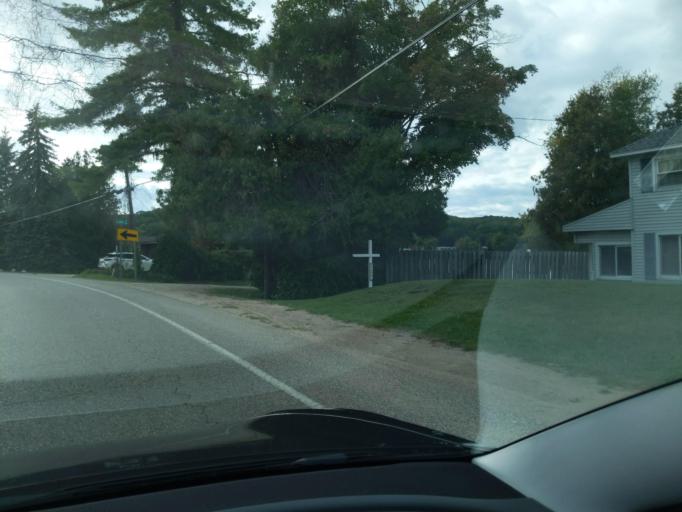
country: US
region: Michigan
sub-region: Kalkaska County
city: Rapid City
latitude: 44.8515
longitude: -85.3238
